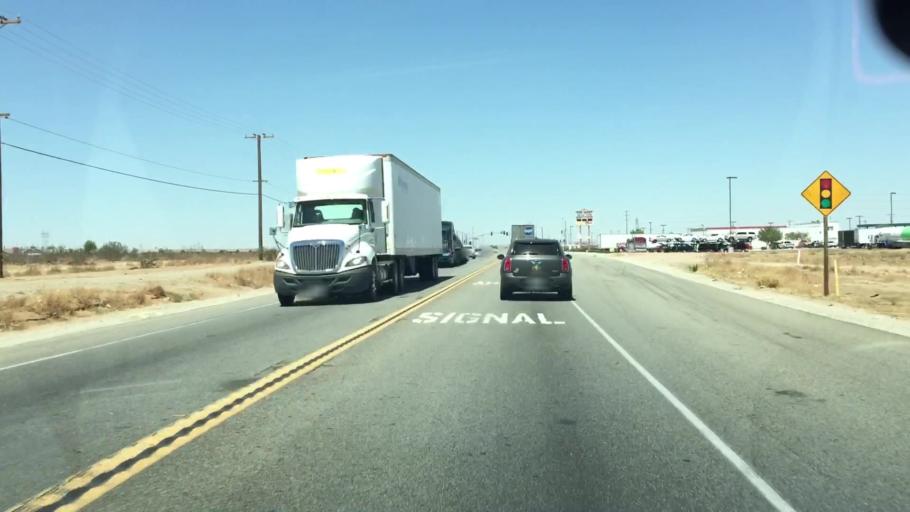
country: US
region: California
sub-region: San Bernardino County
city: Adelanto
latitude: 34.5328
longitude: -117.3994
